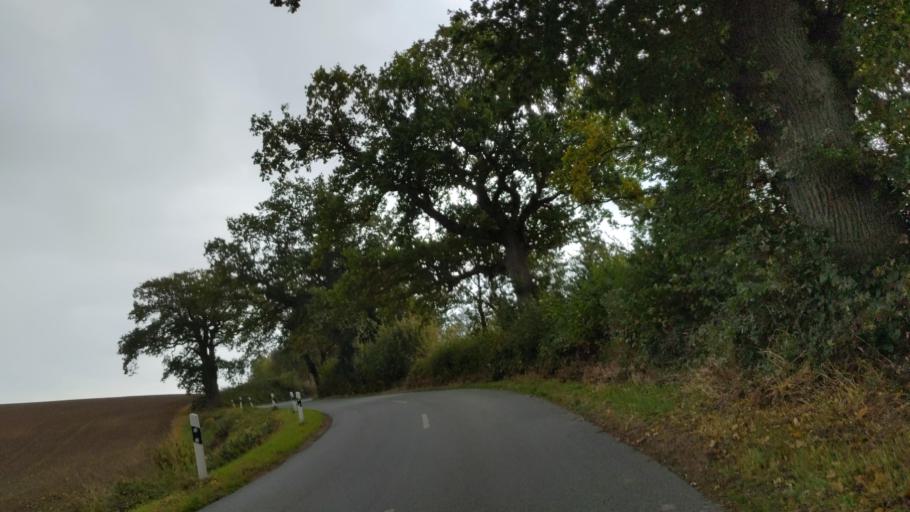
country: DE
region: Schleswig-Holstein
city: Neustadt in Holstein
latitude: 54.1162
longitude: 10.7768
